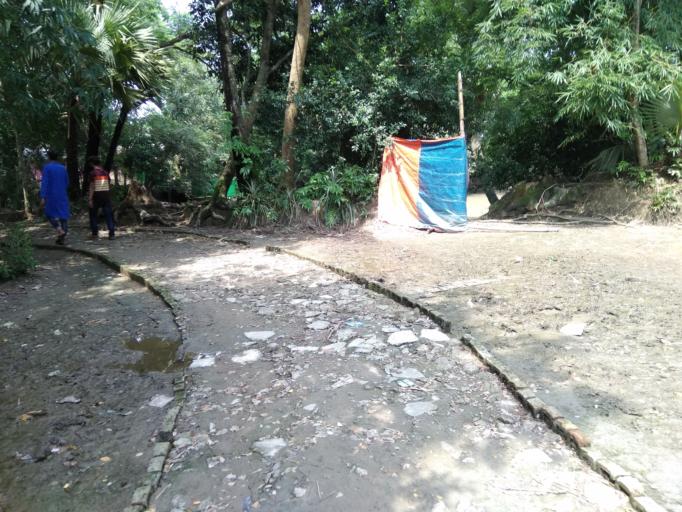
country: BD
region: Chittagong
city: Chhagalnaiya
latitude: 22.8181
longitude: 91.4937
